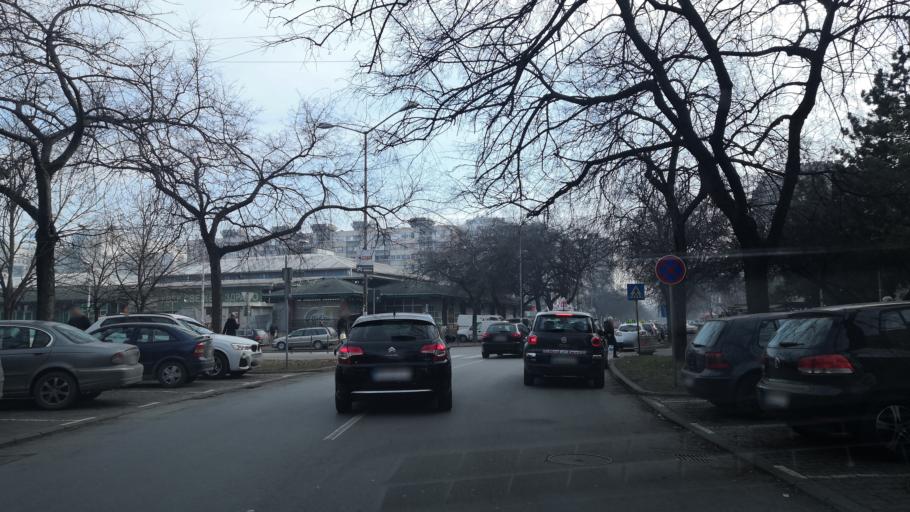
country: RS
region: Autonomna Pokrajina Vojvodina
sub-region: Juznobacki Okrug
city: Novi Sad
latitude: 45.2436
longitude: 19.8358
